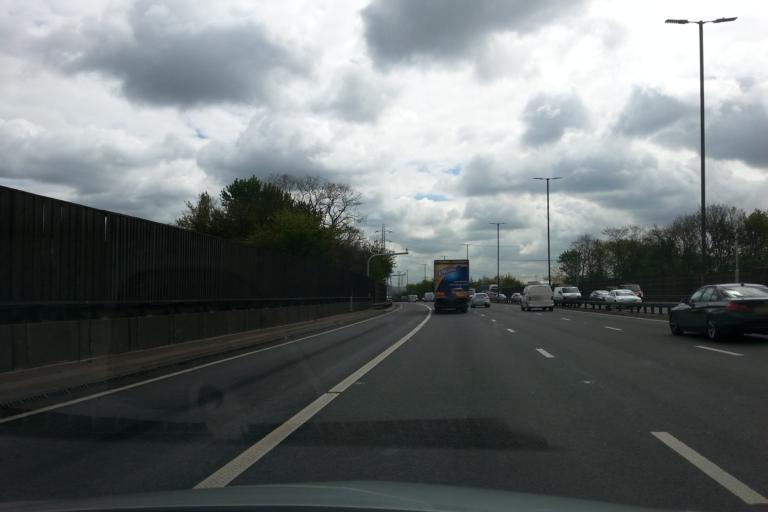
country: GB
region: England
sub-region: City and Borough of Birmingham
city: Hockley
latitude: 52.5289
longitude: -1.8963
